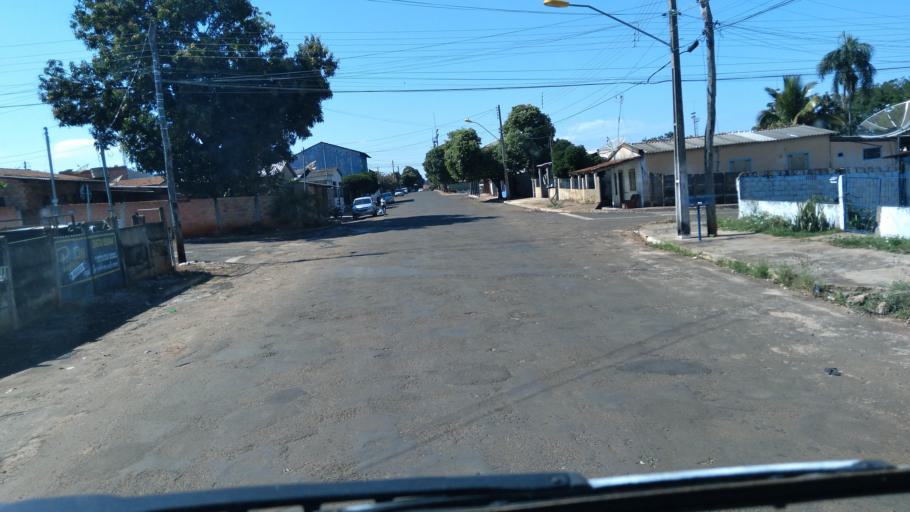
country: BR
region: Goias
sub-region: Mineiros
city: Mineiros
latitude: -17.5722
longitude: -52.5684
